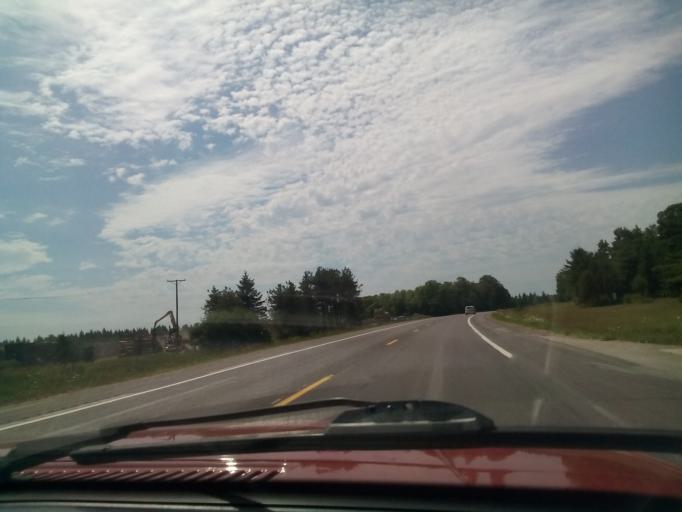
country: US
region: Michigan
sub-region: Schoolcraft County
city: Manistique
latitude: 45.9976
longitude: -86.0048
